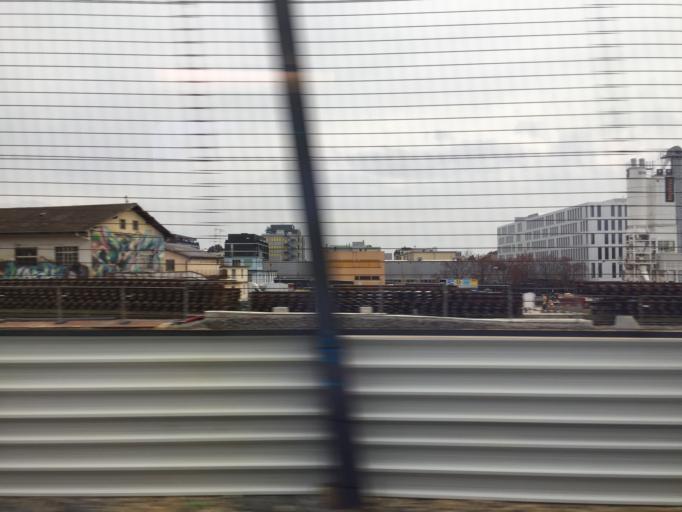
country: CH
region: Vaud
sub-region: Ouest Lausannois District
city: Prilly
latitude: 46.5299
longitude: 6.5941
